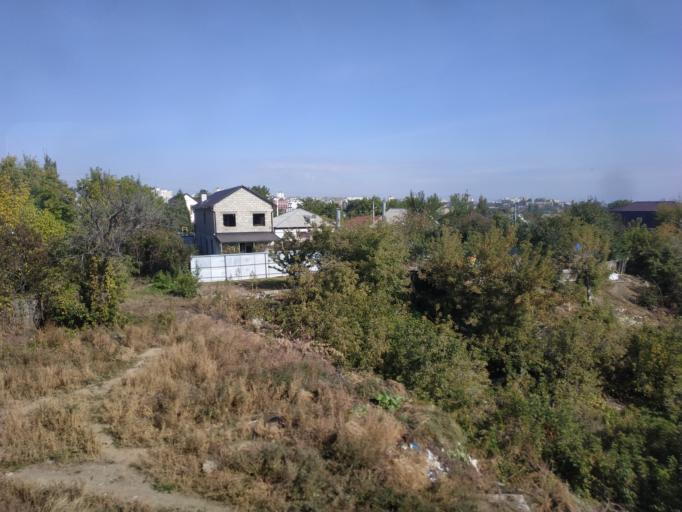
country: RU
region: Volgograd
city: Volgograd
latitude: 48.7494
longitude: 44.5357
